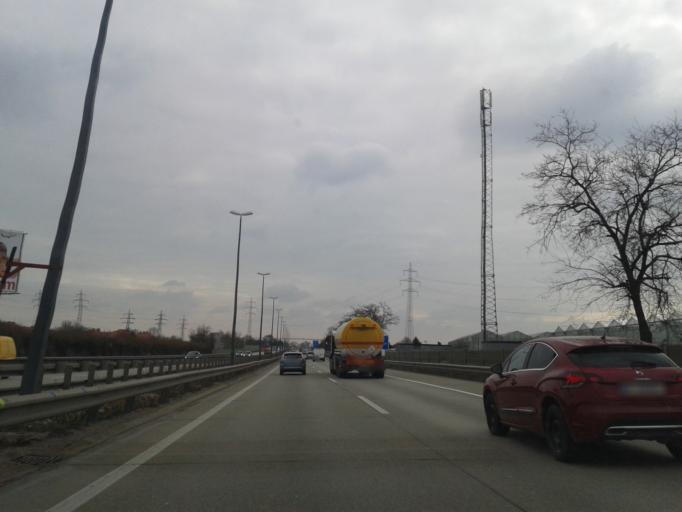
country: AT
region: Lower Austria
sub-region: Politischer Bezirk Wien-Umgebung
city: Schwechat
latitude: 48.1661
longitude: 16.4644
